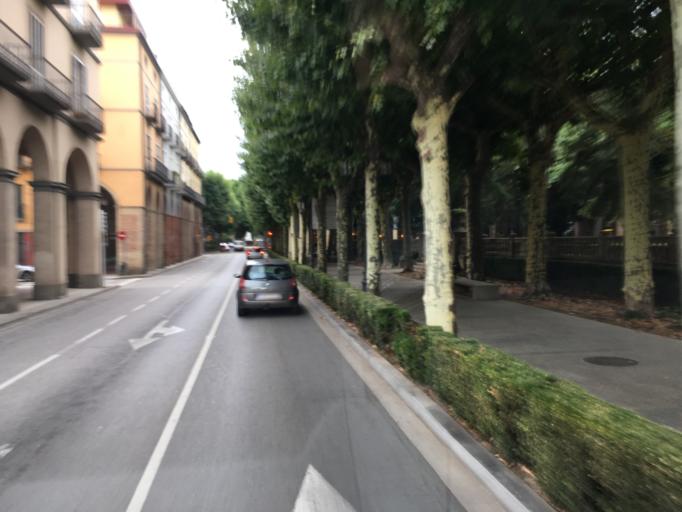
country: ES
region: Catalonia
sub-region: Provincia de Girona
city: Olot
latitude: 42.1806
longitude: 2.4857
